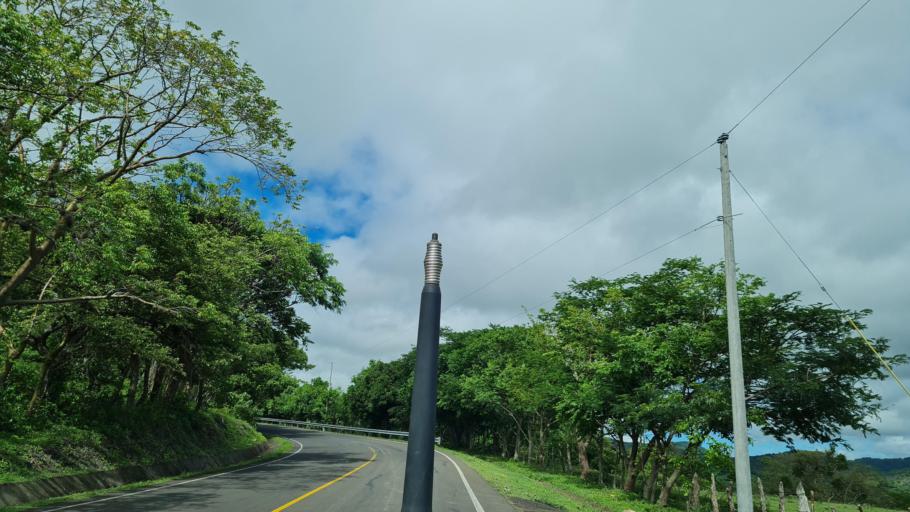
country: NI
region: Boaco
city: San Jose de los Remates
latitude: 12.6093
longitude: -85.8965
